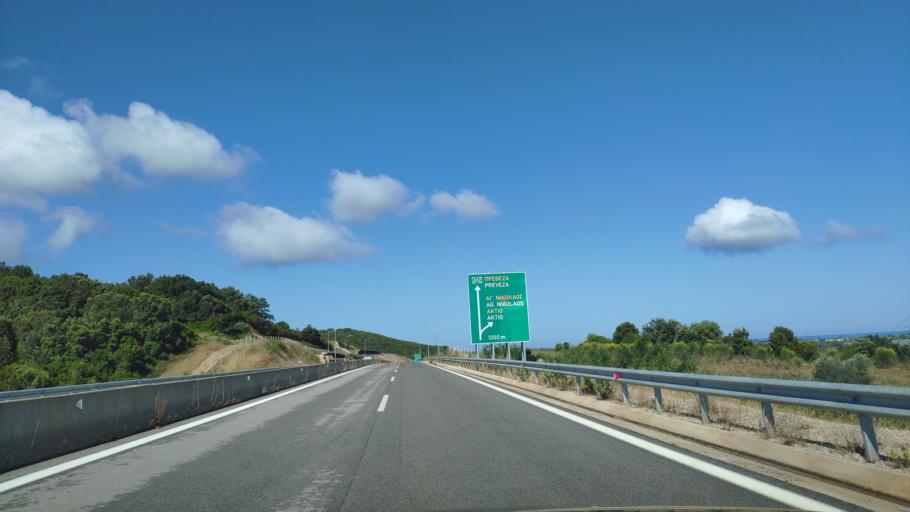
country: GR
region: West Greece
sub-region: Nomos Aitolias kai Akarnanias
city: Vonitsa
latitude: 38.9149
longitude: 20.8184
